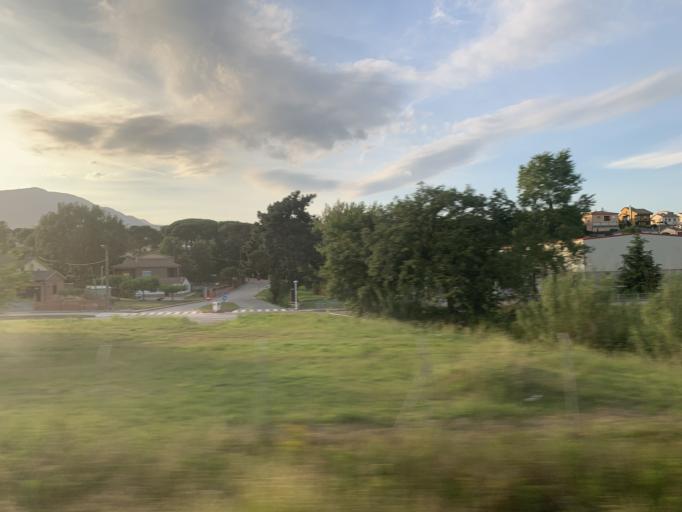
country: ES
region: Catalonia
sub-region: Provincia de Girona
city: Breda
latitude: 41.7235
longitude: 2.5562
